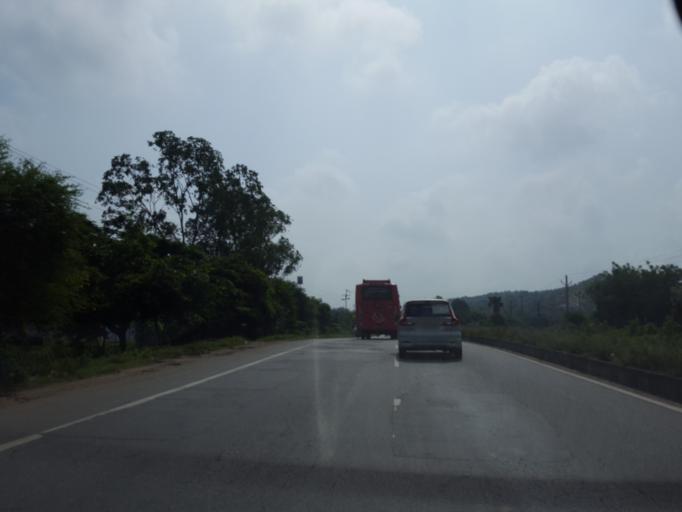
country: IN
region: Telangana
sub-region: Rangareddi
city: Ghatkesar
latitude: 17.2880
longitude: 78.7706
